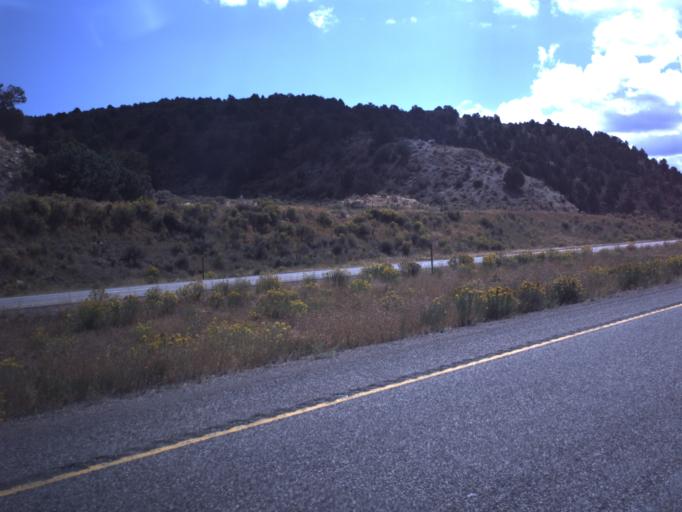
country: US
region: Utah
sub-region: Sevier County
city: Salina
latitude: 38.8276
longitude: -111.5393
